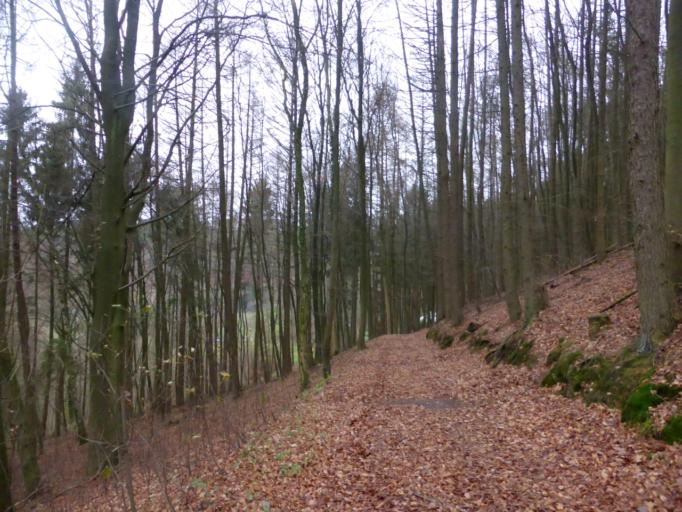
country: LU
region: Luxembourg
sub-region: Canton de Mersch
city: Lorentzweiler
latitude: 49.6826
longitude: 6.1453
